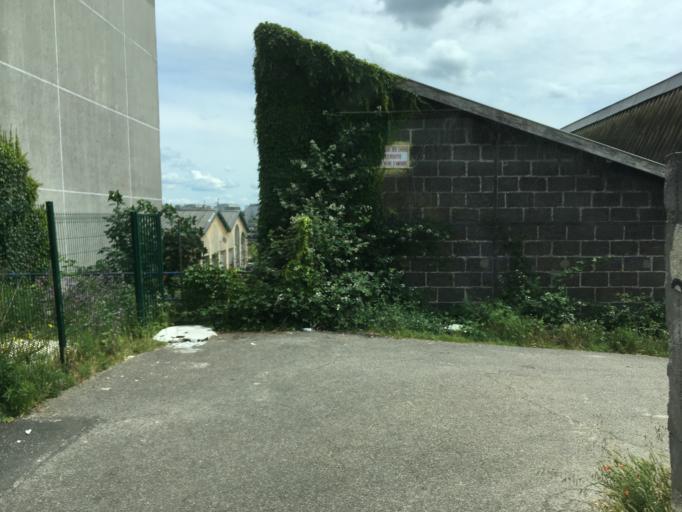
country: FR
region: Aquitaine
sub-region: Departement de la Gironde
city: Begles
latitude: 44.8193
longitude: -0.5626
